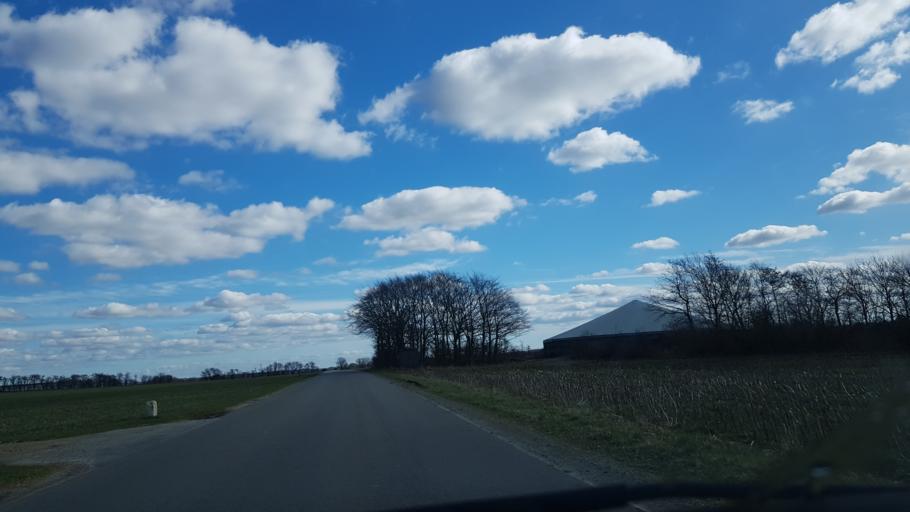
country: DK
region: South Denmark
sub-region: Vejen Kommune
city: Rodding
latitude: 55.3953
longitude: 9.0184
